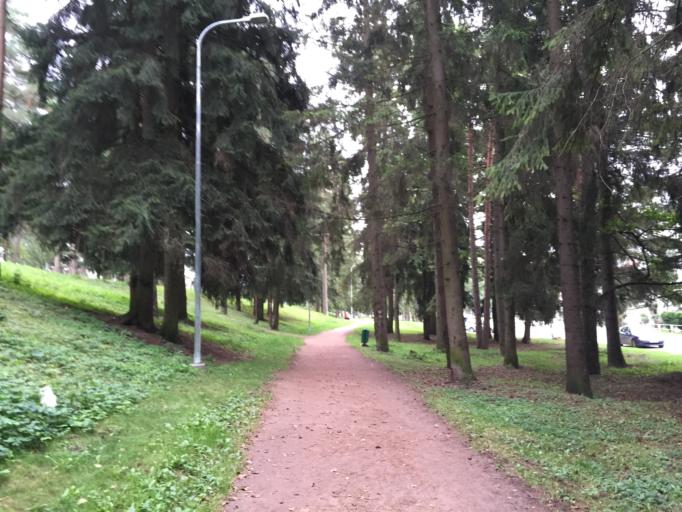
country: LV
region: Ogre
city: Ogre
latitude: 56.8256
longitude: 24.5961
